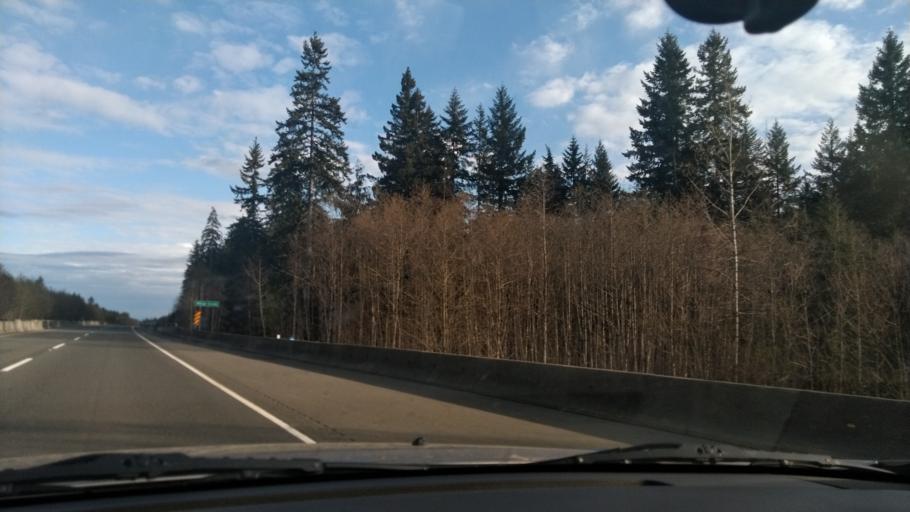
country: CA
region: British Columbia
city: Courtenay
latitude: 49.7602
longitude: -125.1315
